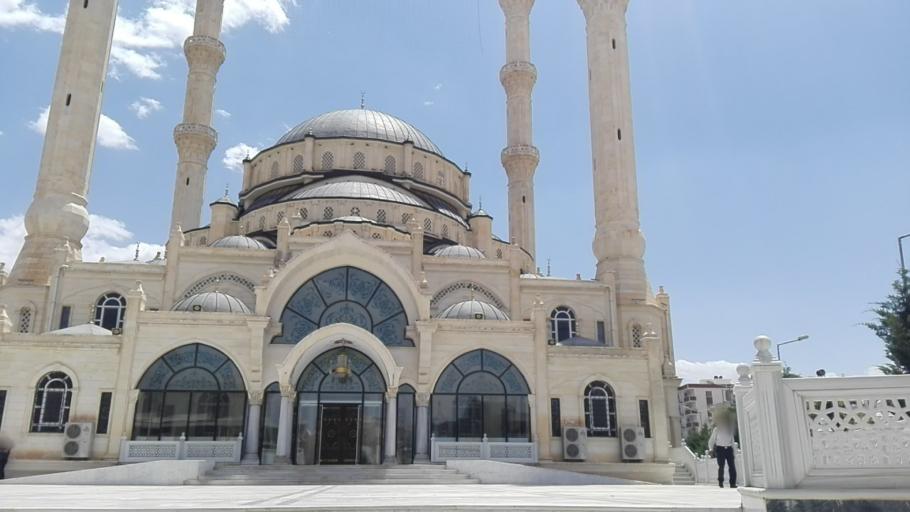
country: TR
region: Mardin
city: Midyat
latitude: 37.4193
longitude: 41.3615
